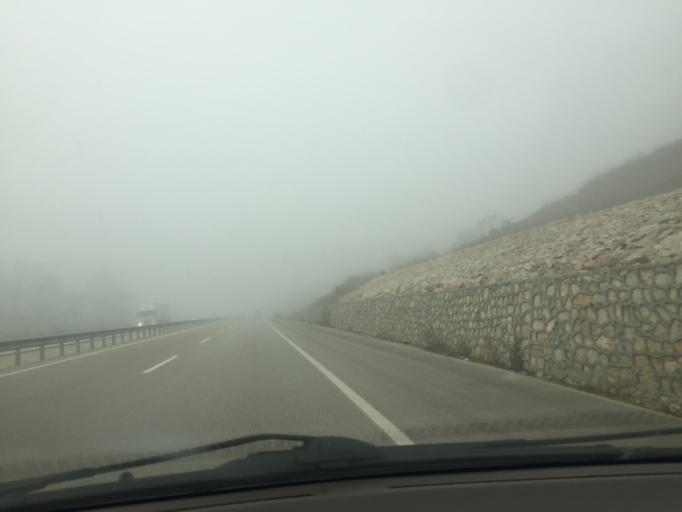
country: TR
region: Canakkale
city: Can
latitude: 40.0594
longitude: 27.1336
